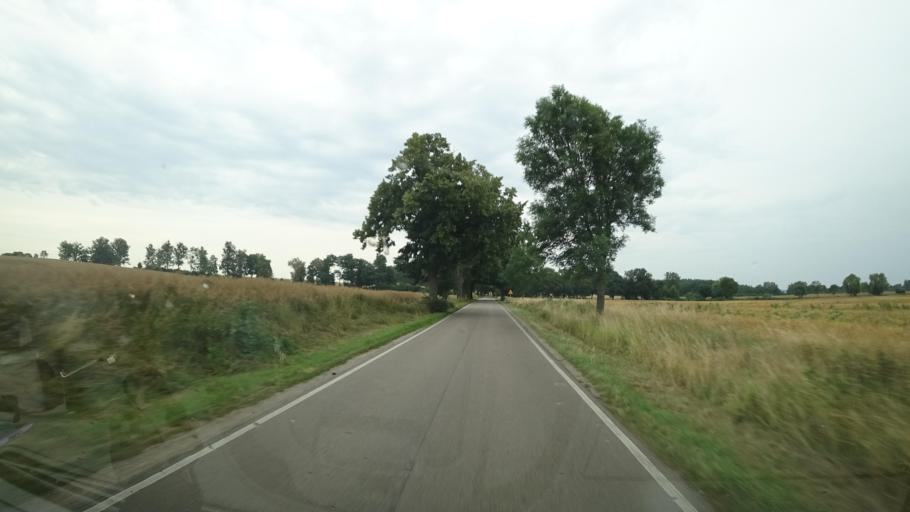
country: PL
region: Warmian-Masurian Voivodeship
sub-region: Powiat gizycki
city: Ryn
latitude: 53.9016
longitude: 21.5679
